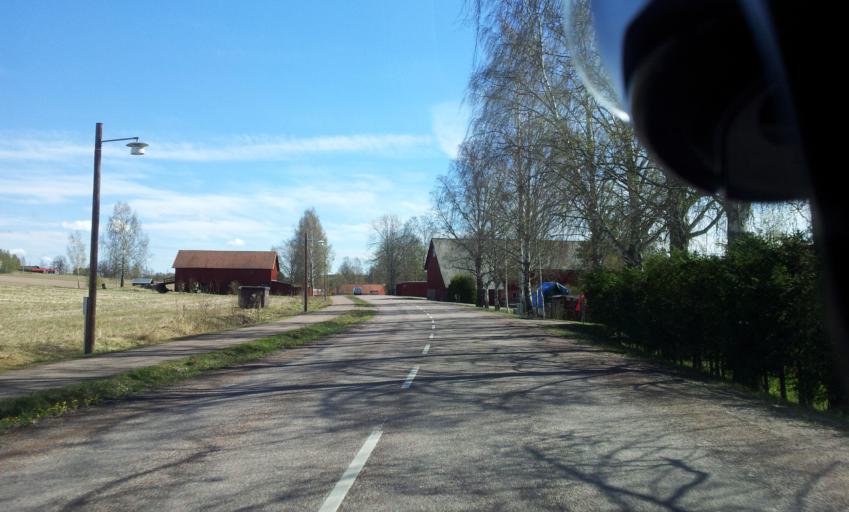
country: SE
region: Dalarna
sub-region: Borlange Kommun
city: Ornas
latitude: 60.4621
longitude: 15.5291
